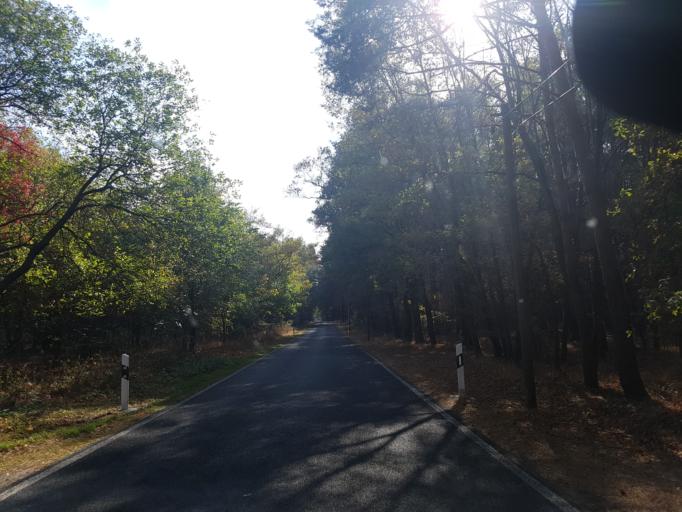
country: DE
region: Brandenburg
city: Lebusa
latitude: 51.8247
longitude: 13.3928
